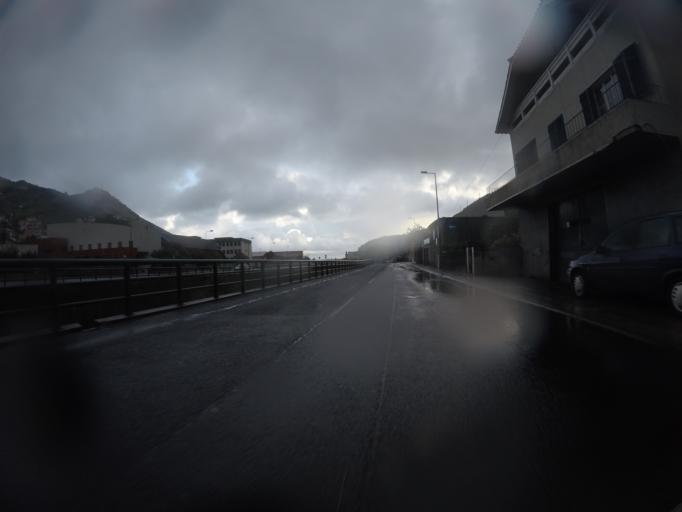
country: PT
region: Madeira
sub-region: Machico
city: Machico
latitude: 32.7267
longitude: -16.7726
